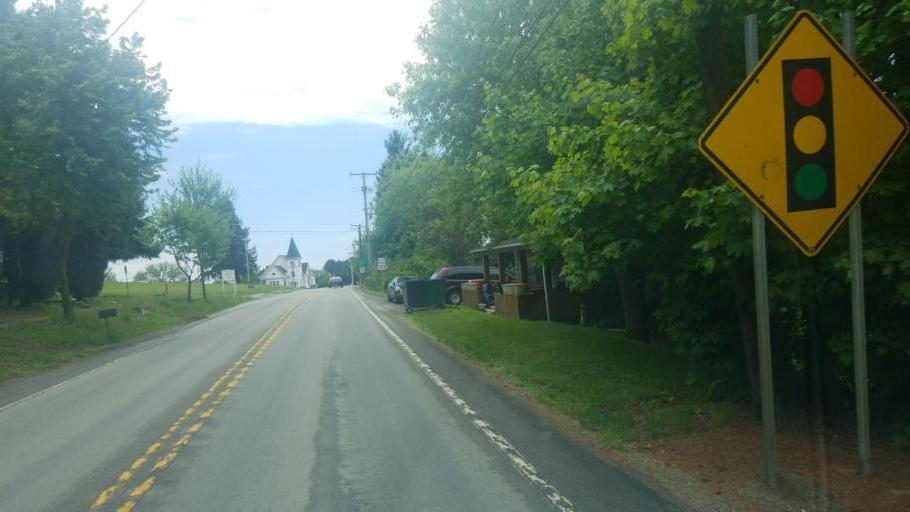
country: US
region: Pennsylvania
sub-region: Clarion County
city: Marianne
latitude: 41.2526
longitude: -79.4595
